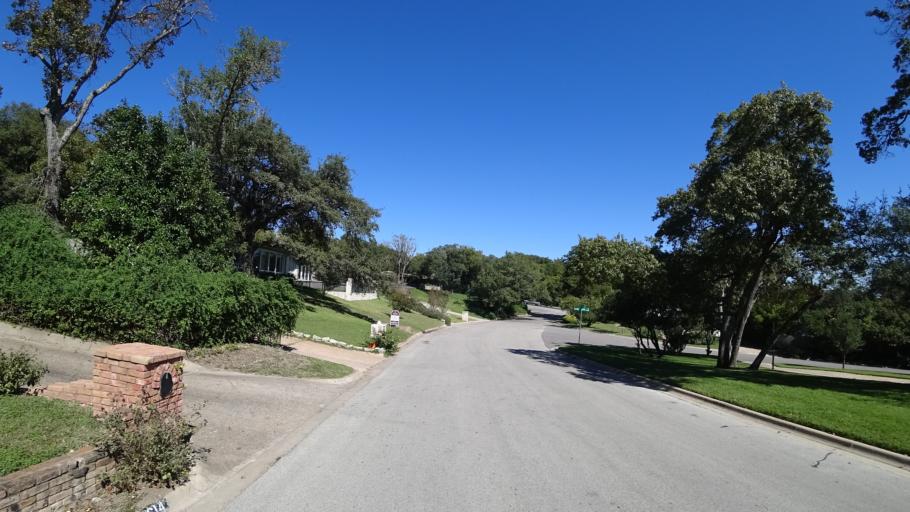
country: US
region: Texas
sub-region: Travis County
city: West Lake Hills
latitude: 30.3302
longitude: -97.7673
